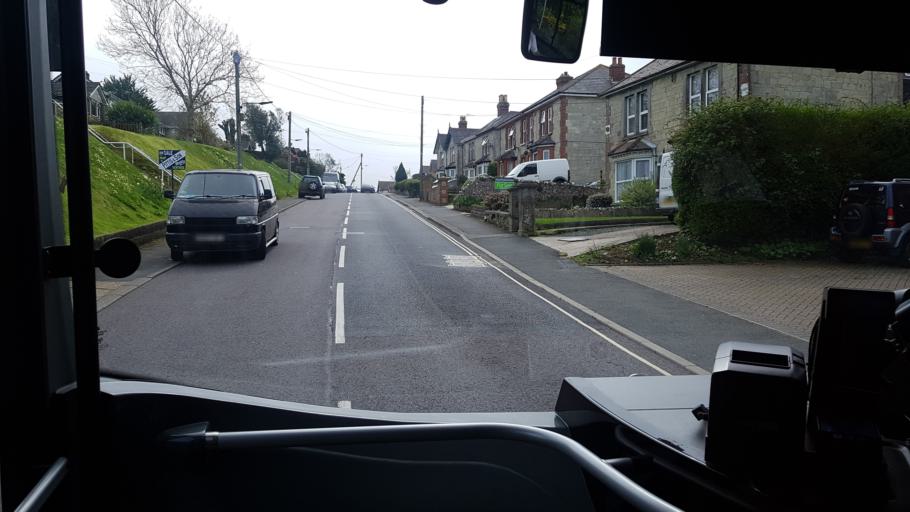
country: GB
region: England
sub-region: Isle of Wight
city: Ventnor
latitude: 50.6134
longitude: -1.2232
